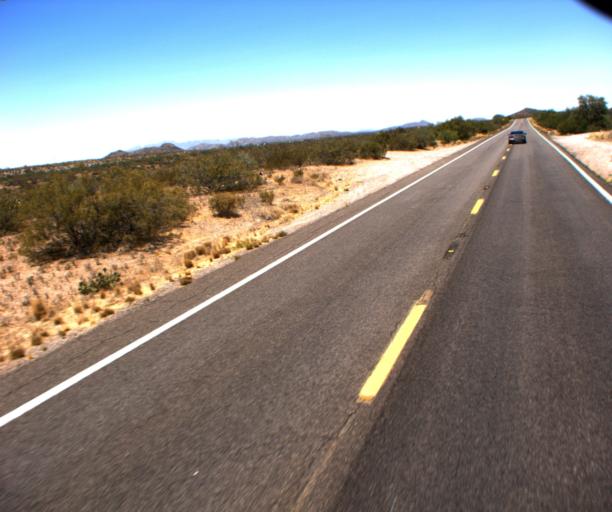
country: US
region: Arizona
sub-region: Pima County
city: Catalina
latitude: 32.6405
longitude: -111.0142
